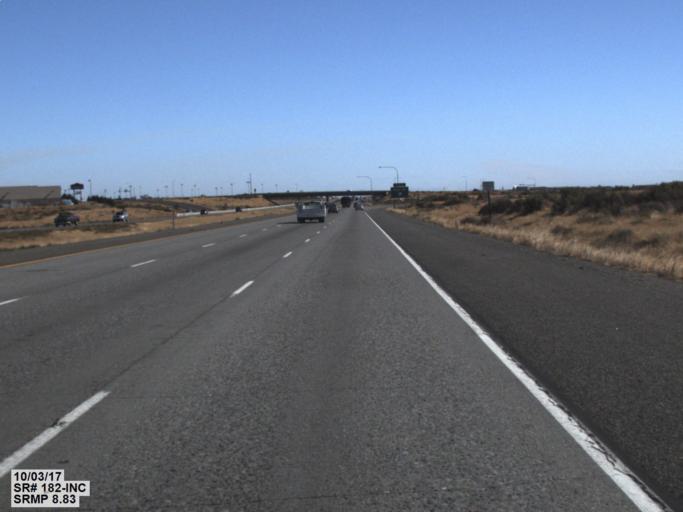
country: US
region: Washington
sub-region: Franklin County
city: West Pasco
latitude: 46.2684
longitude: -119.1920
